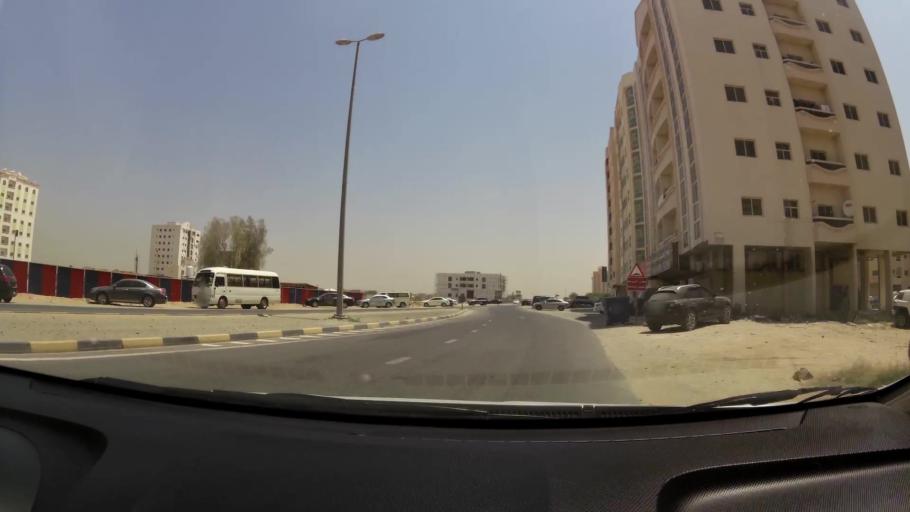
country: AE
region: Ajman
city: Ajman
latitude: 25.4084
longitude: 55.5136
